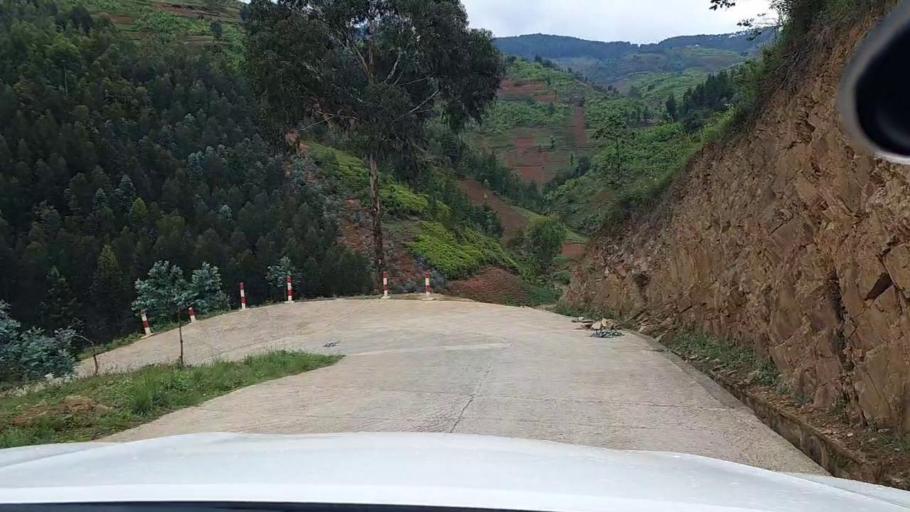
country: RW
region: Western Province
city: Kibuye
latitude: -2.1268
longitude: 29.4277
